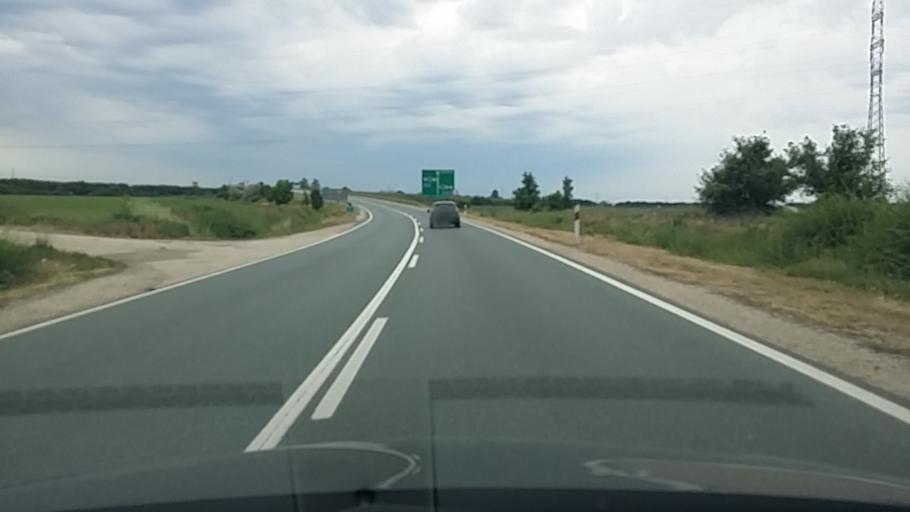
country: HU
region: Fejer
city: dunaujvaros
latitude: 46.9918
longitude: 18.8928
